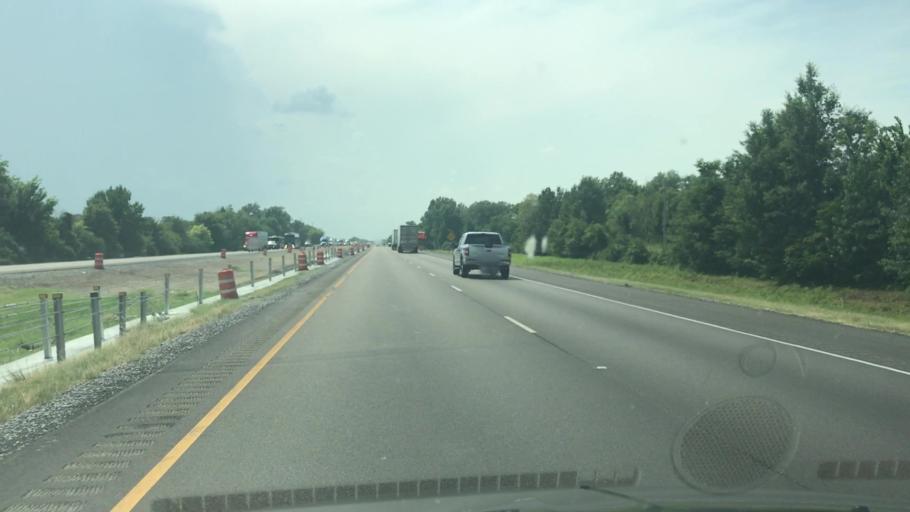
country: US
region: Arkansas
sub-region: Crittenden County
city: Earle
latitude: 35.1341
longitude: -90.4482
